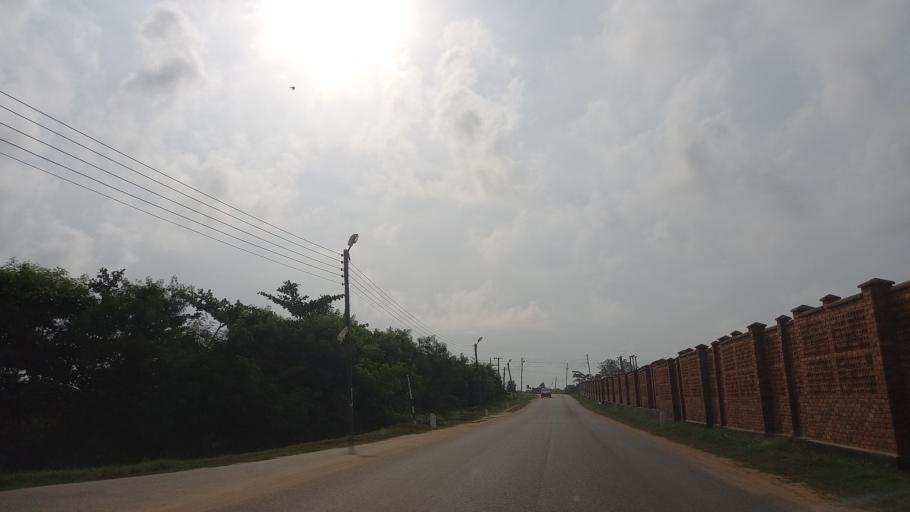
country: GH
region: Western
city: Shama Junction
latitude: 4.9751
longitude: -1.6568
